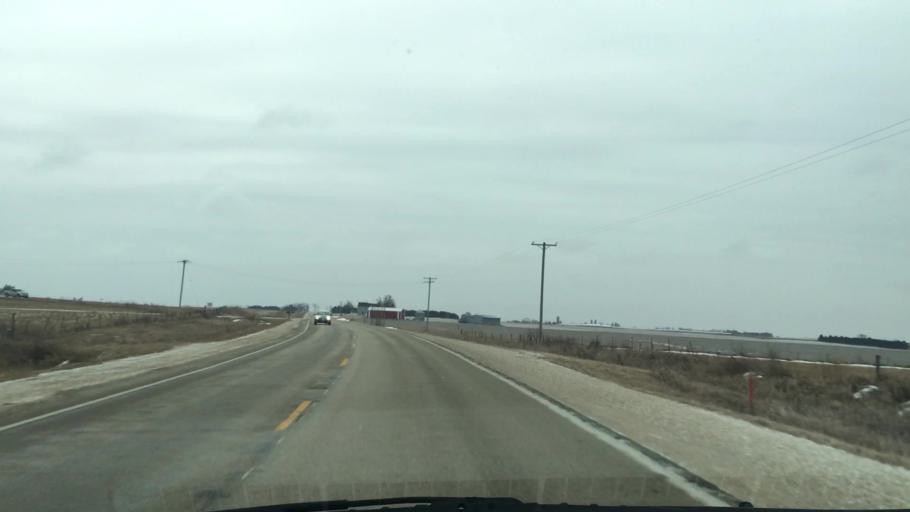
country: US
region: Iowa
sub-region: Fayette County
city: West Union
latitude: 43.0326
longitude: -91.8360
